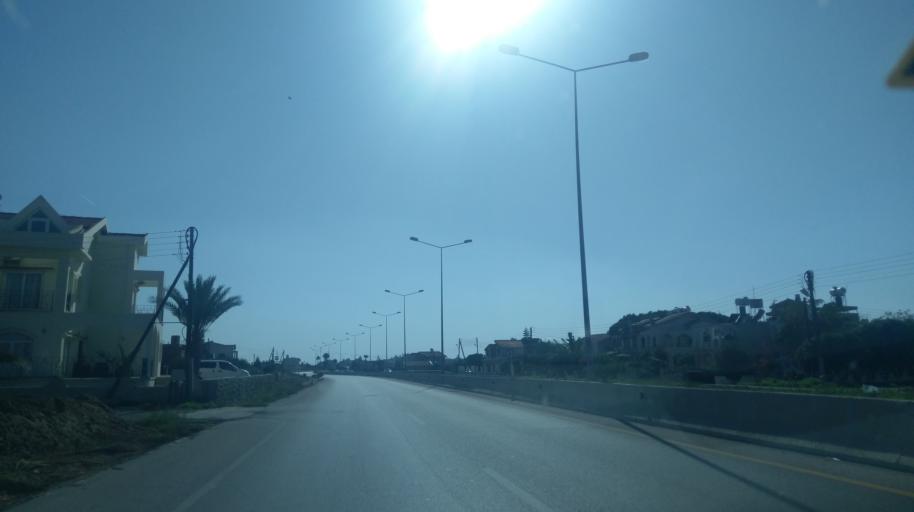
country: CY
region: Ammochostos
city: Trikomo
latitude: 35.2202
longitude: 33.8944
